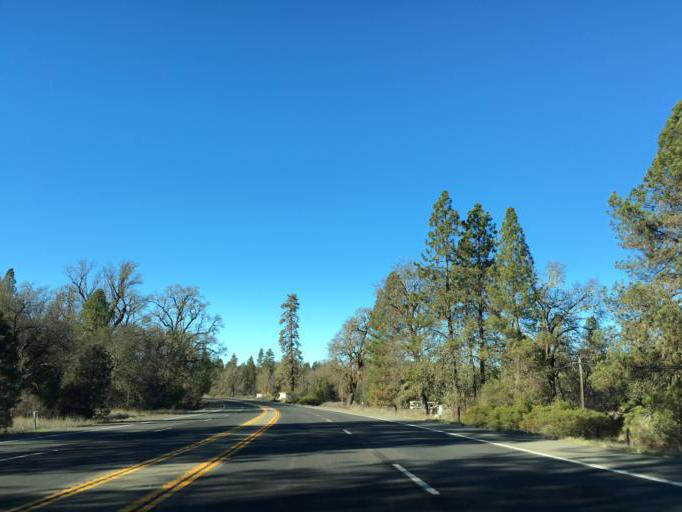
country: US
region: California
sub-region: Mendocino County
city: Laytonville
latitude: 39.7269
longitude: -123.5045
